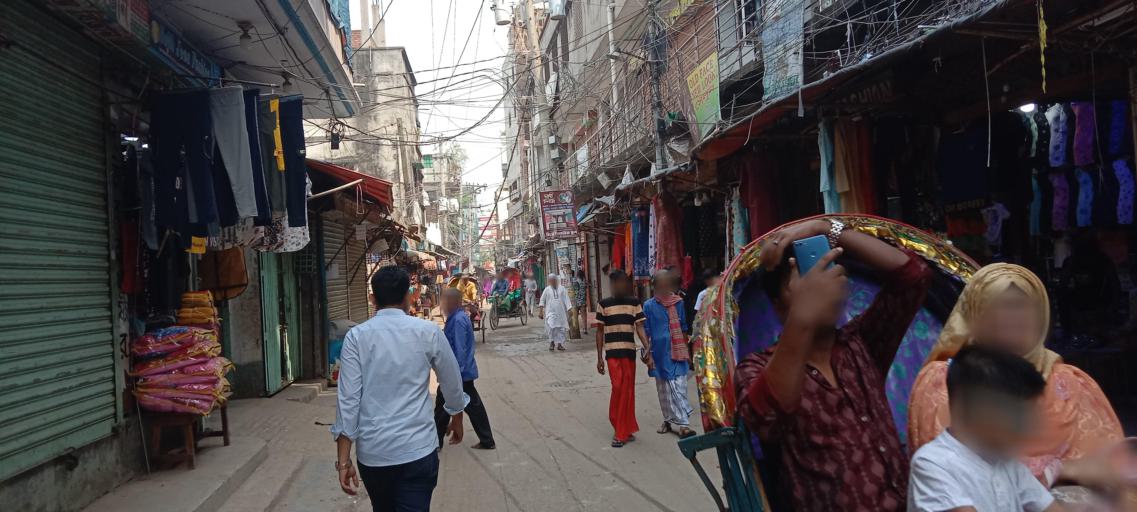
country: BD
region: Dhaka
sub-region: Dhaka
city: Dhaka
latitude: 23.7081
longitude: 90.3979
